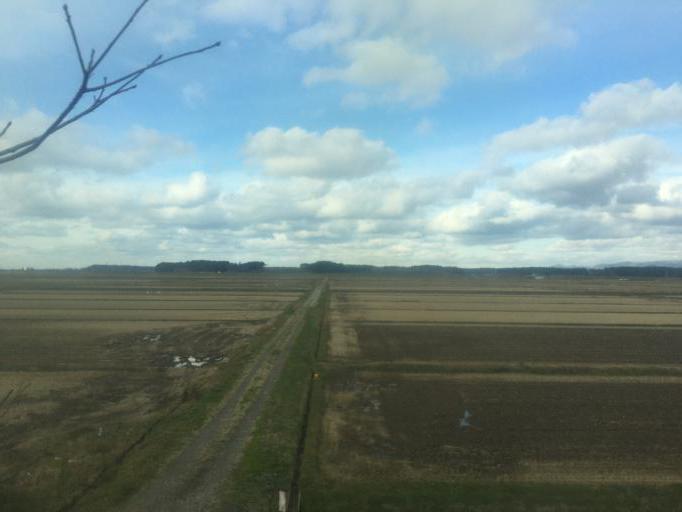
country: JP
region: Akita
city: Noshiromachi
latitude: 40.2020
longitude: 140.1066
